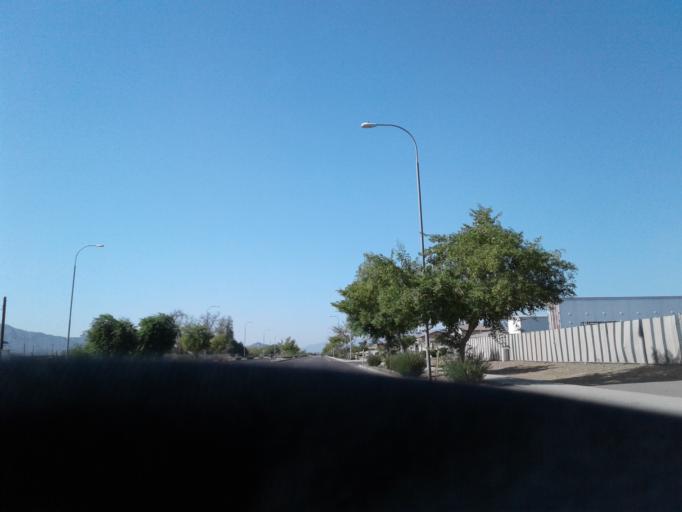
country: US
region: Arizona
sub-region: Maricopa County
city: Laveen
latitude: 33.3999
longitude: -112.1684
